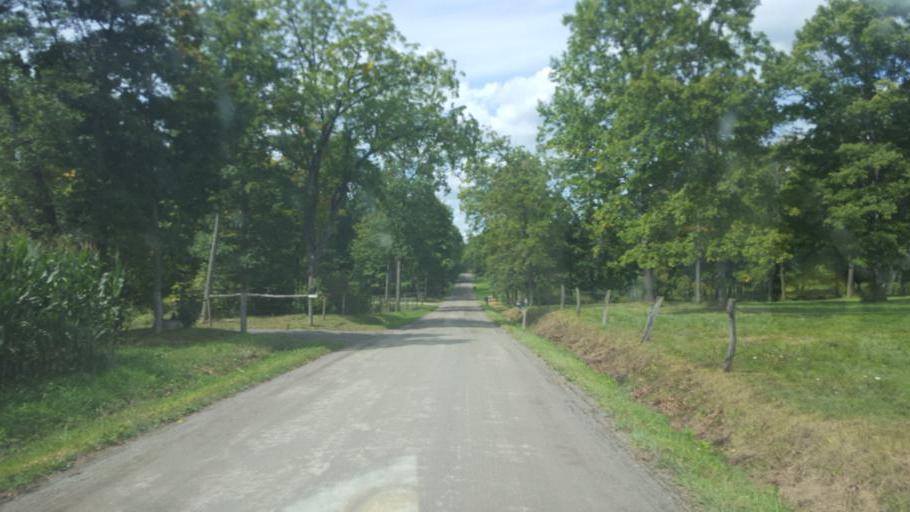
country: US
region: Ohio
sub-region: Geauga County
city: Middlefield
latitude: 41.4259
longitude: -80.9933
